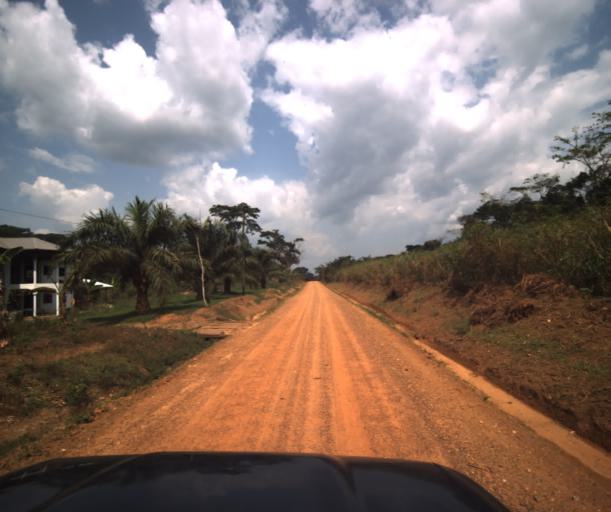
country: CM
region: Centre
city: Akono
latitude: 3.5582
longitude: 11.0751
